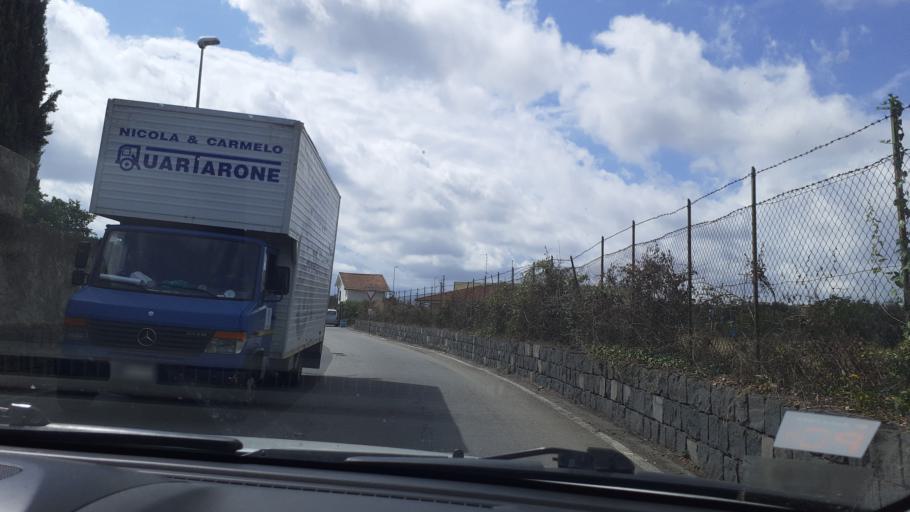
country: IT
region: Sicily
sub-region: Catania
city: San Giovanni la Punta
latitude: 37.5882
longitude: 15.0910
